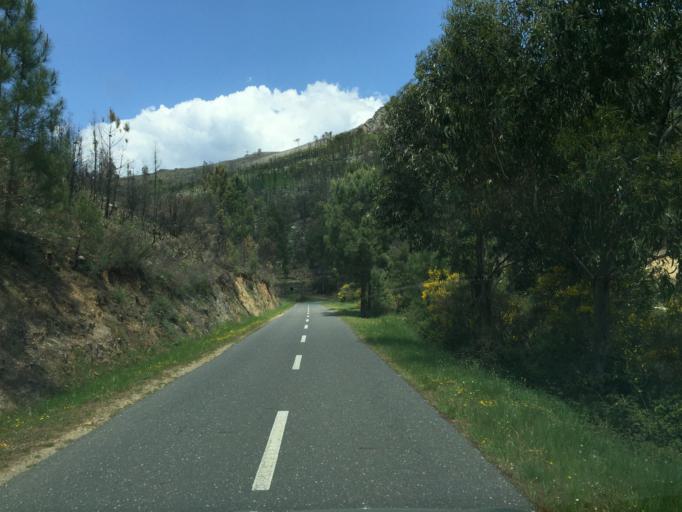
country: PT
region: Coimbra
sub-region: Pampilhosa da Serra
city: Pampilhosa da Serra
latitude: 40.0916
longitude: -7.8697
